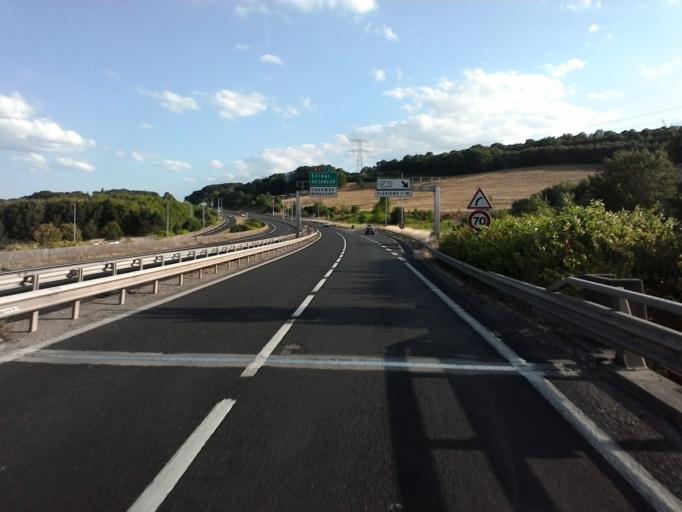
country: FR
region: Lorraine
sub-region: Departement de Meurthe-et-Moselle
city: Richardmenil
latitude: 48.5781
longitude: 6.1748
